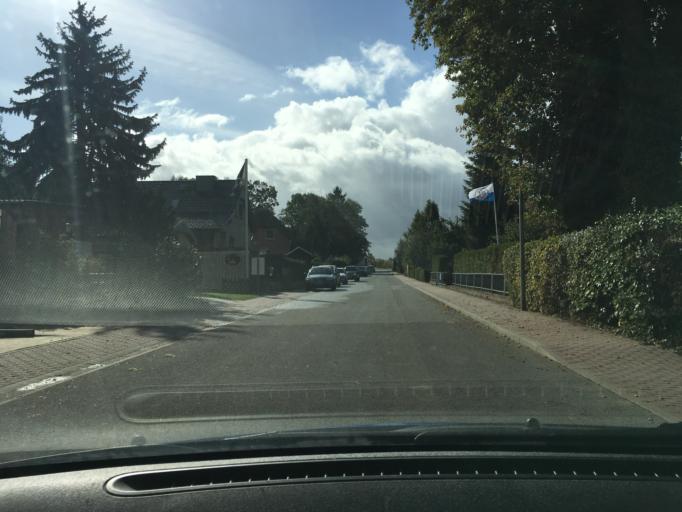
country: DE
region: Saxony-Anhalt
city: Salzwedel
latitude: 52.8635
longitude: 11.1184
